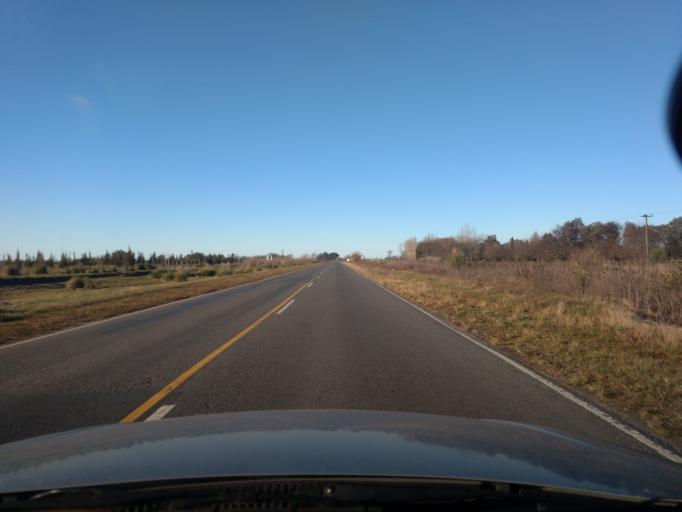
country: AR
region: Buenos Aires
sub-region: Partido de Lujan
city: Lujan
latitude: -34.6598
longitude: -59.1011
